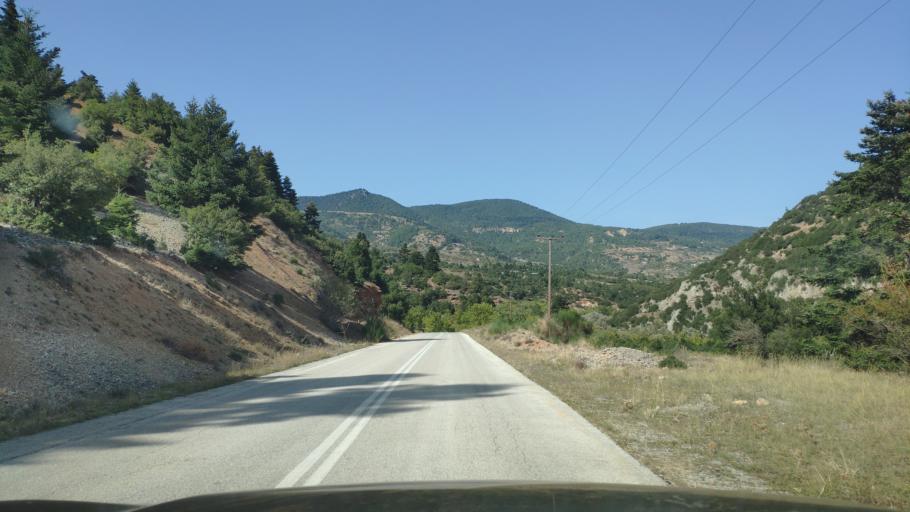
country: GR
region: West Greece
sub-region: Nomos Achaias
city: Aiyira
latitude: 37.9750
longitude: 22.3541
